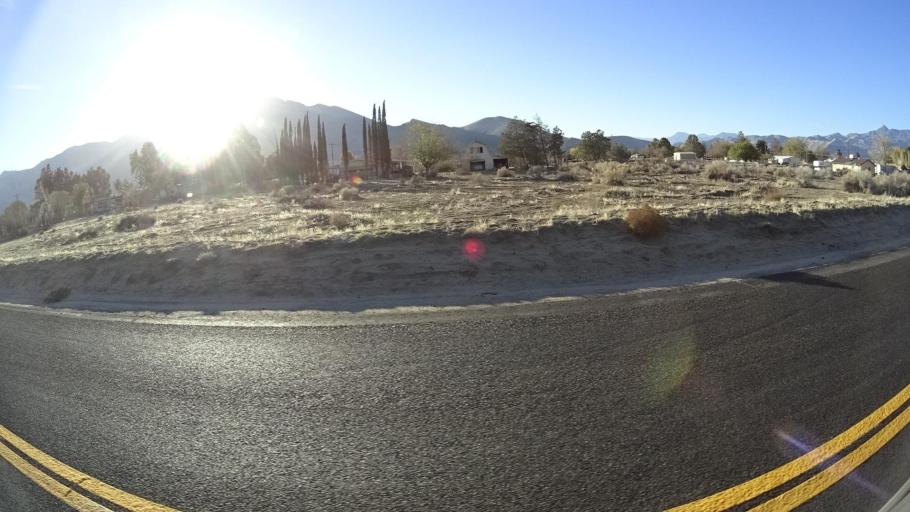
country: US
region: California
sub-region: Kern County
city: Weldon
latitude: 35.6423
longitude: -118.2492
